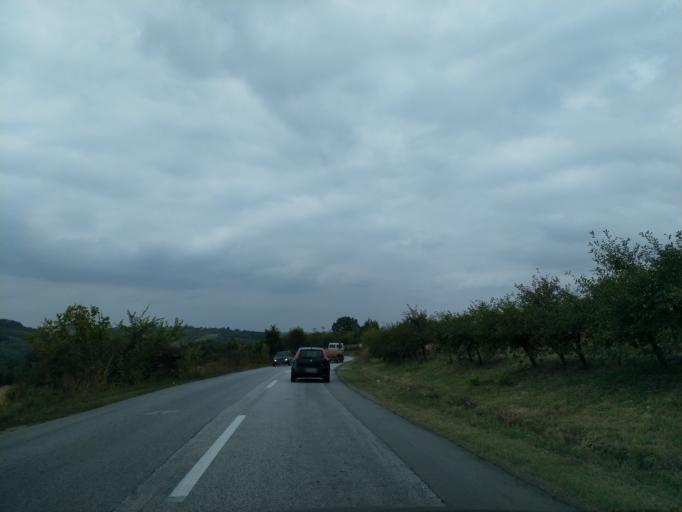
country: RS
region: Central Serbia
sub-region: Sumadijski Okrug
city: Topola
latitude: 44.1998
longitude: 20.7278
